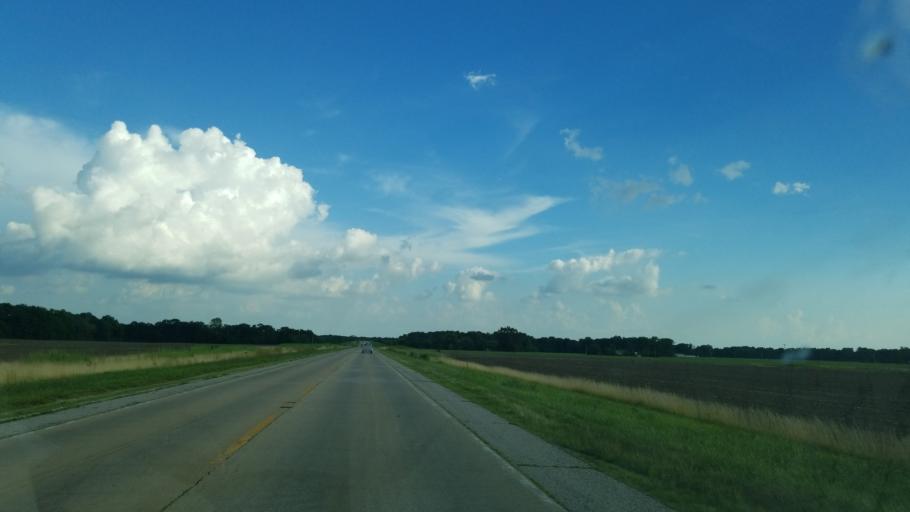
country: US
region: Illinois
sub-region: Marion County
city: Sandoval
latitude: 38.5900
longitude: -89.1084
